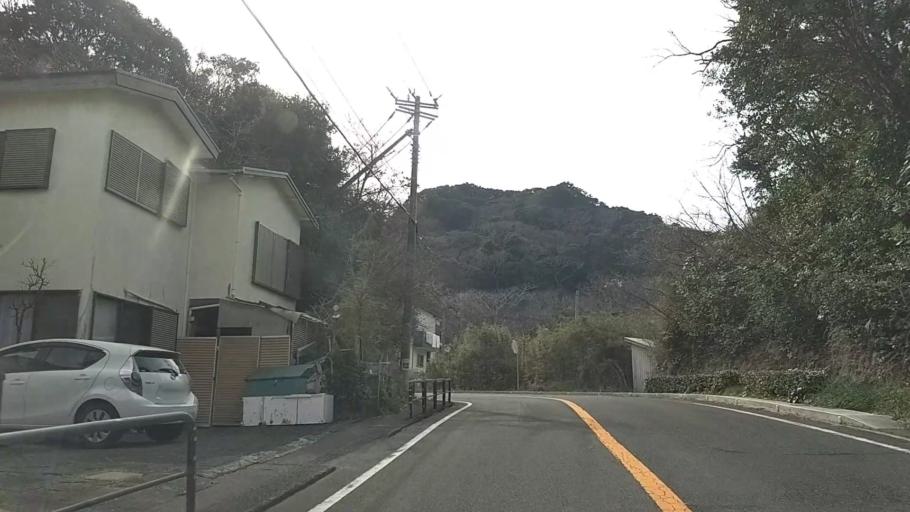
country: JP
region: Shizuoka
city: Shimoda
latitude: 34.6710
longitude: 138.9644
